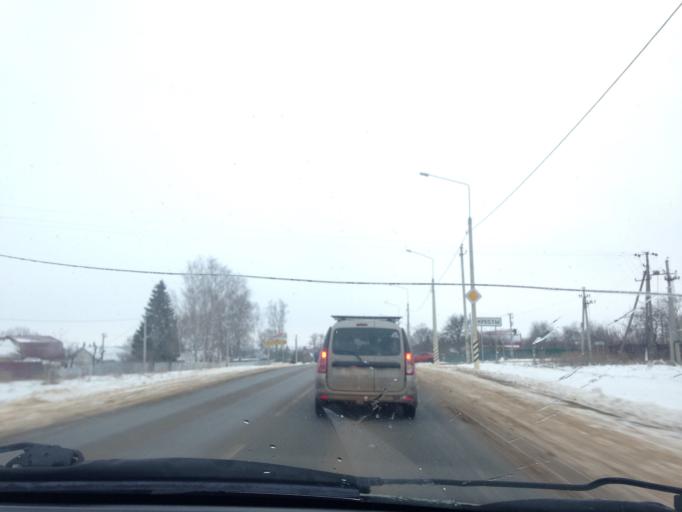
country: RU
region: Tula
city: Shchekino
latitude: 53.9814
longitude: 37.5023
